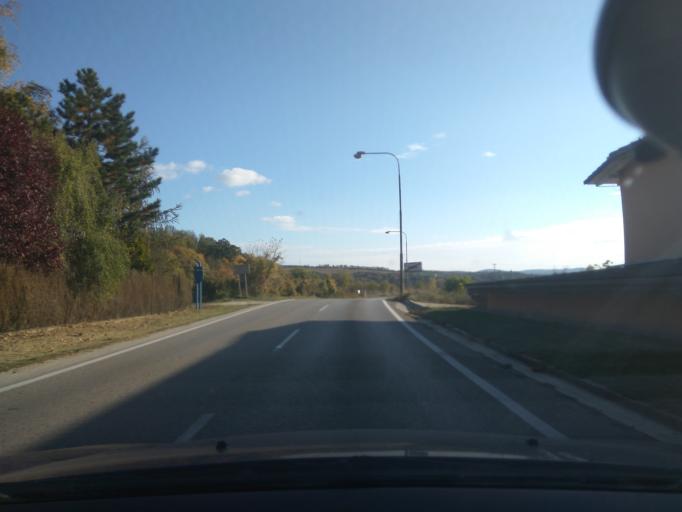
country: SK
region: Trnavsky
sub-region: Okres Trnava
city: Piestany
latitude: 48.5739
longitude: 17.8364
